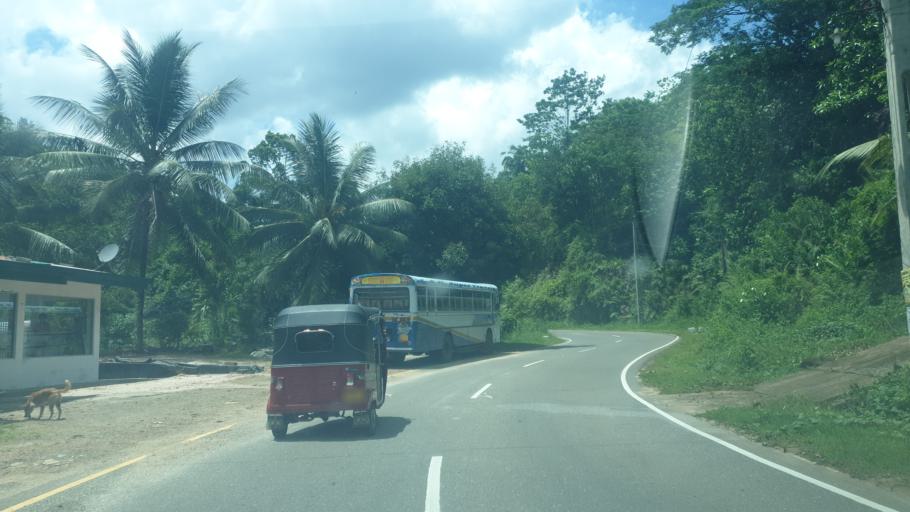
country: LK
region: Western
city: Horawala Junction
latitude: 6.5425
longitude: 80.2744
